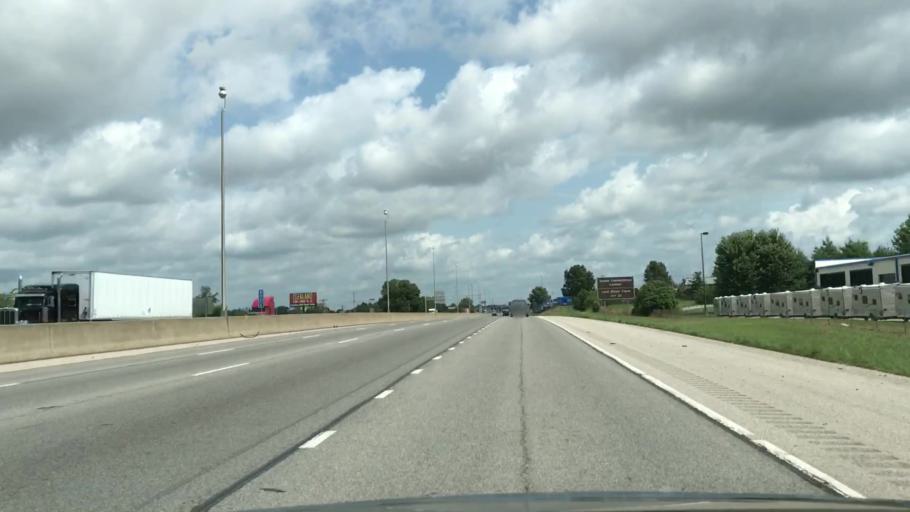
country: US
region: Kentucky
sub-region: Warren County
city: Plano
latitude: 36.9236
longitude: -86.4242
